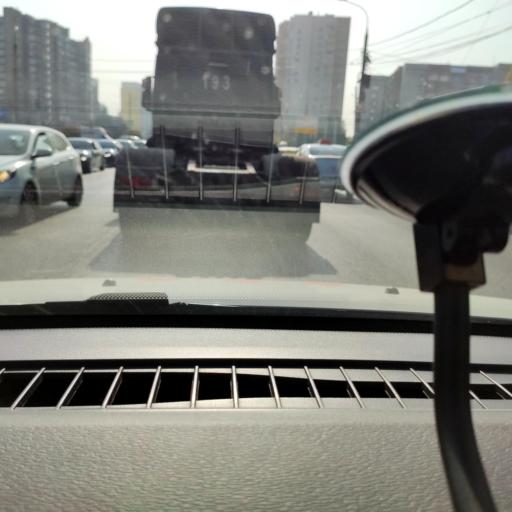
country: RU
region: Samara
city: Samara
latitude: 53.2136
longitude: 50.2122
